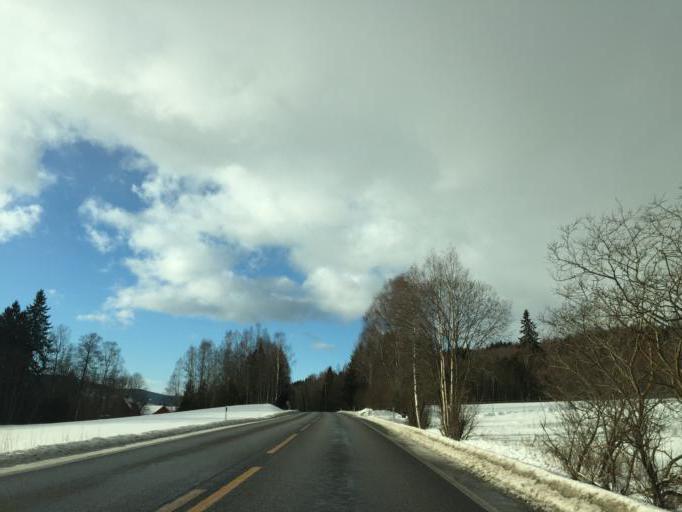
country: NO
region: Hedmark
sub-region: Kongsvinger
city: Spetalen
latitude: 60.2140
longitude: 11.9206
